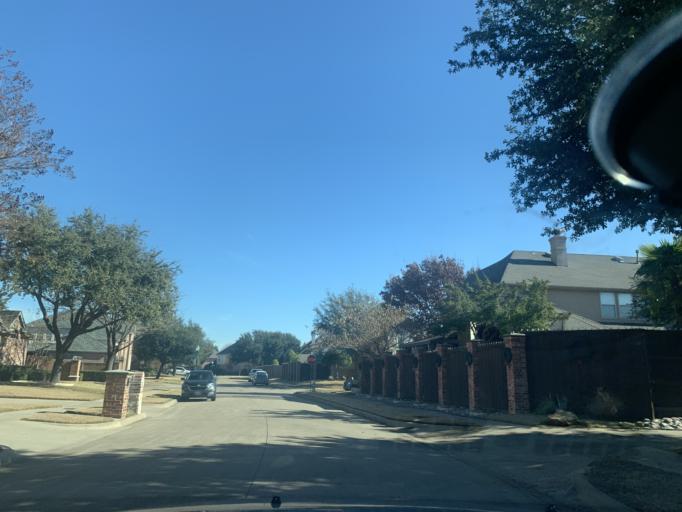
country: US
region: Texas
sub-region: Denton County
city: The Colony
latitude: 33.0542
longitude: -96.8243
